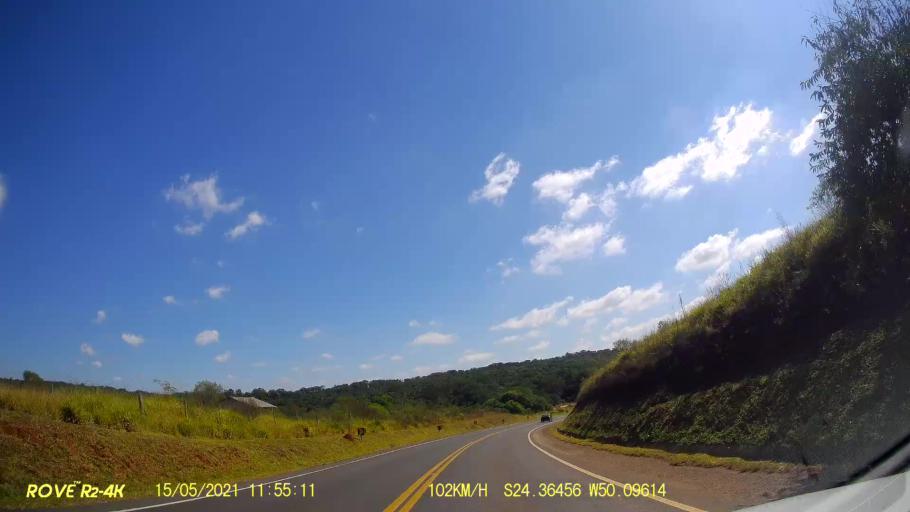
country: BR
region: Parana
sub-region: Pirai Do Sul
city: Pirai do Sul
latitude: -24.3646
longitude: -50.0963
